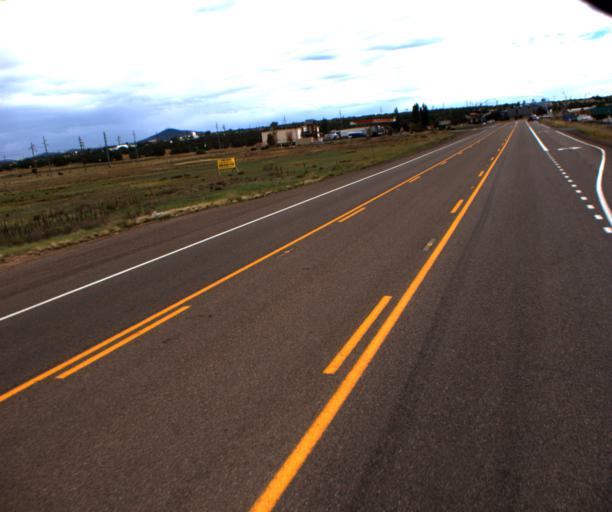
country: US
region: Arizona
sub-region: Navajo County
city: Show Low
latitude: 34.2598
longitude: -110.0191
